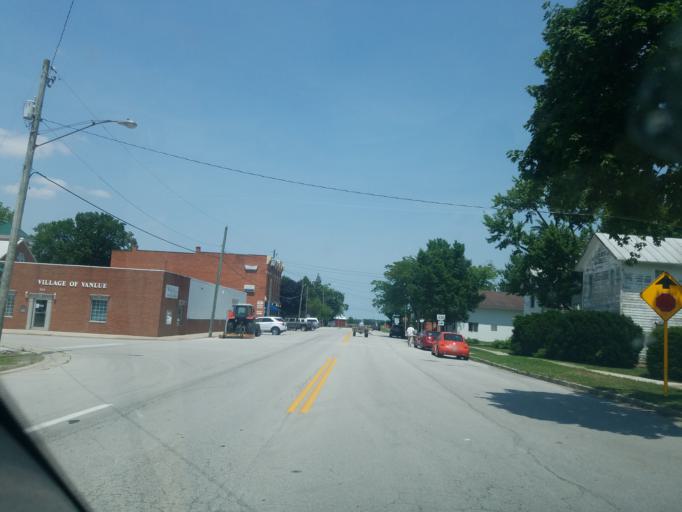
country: US
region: Ohio
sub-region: Wyandot County
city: Carey
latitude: 40.9745
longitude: -83.4801
